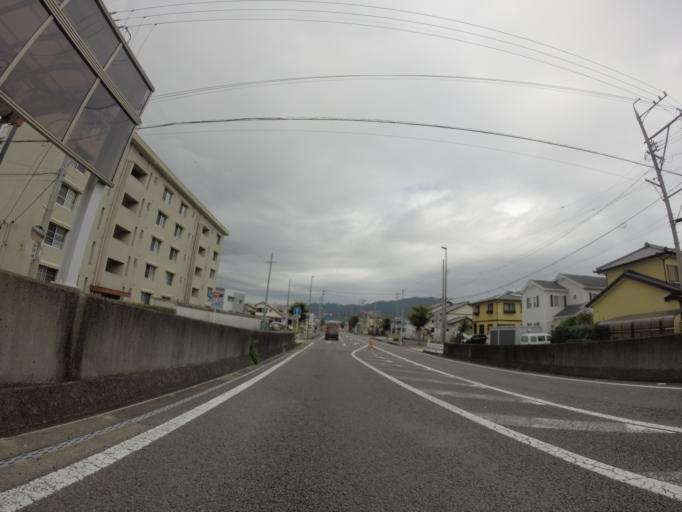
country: JP
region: Shizuoka
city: Yaizu
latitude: 34.8683
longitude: 138.3068
